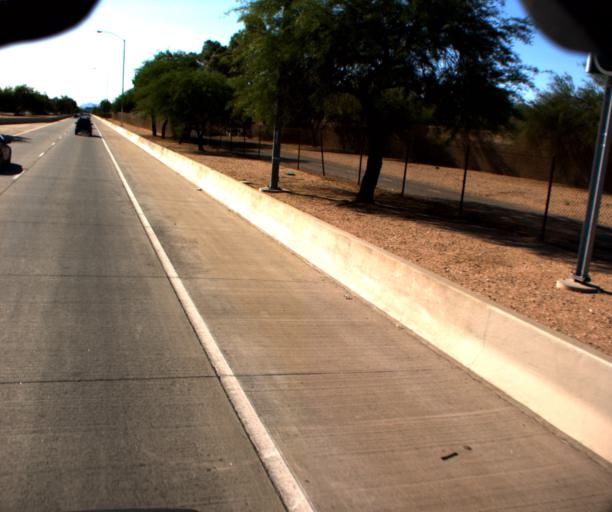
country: US
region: Arizona
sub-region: Pima County
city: Tucson
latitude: 32.2004
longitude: -110.9309
